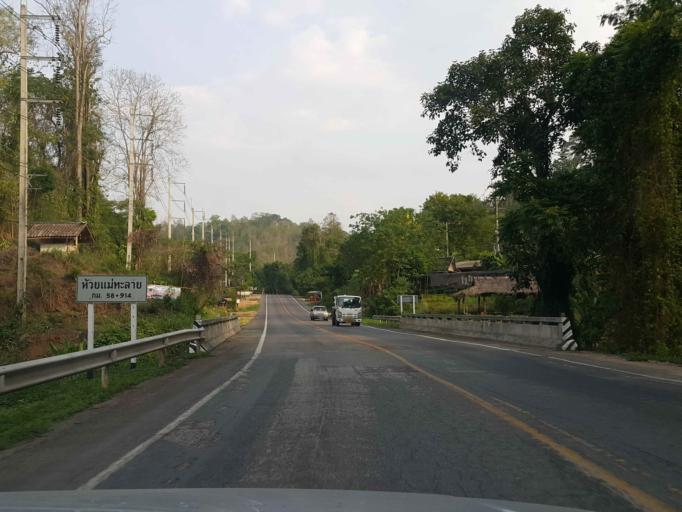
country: TH
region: Chiang Mai
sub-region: Amphoe Chiang Dao
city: Chiang Dao
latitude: 19.2636
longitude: 98.9687
